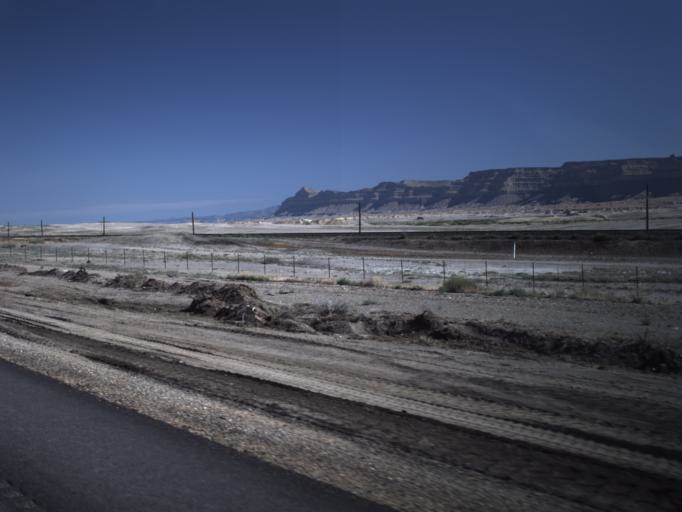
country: US
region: Utah
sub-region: Carbon County
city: East Carbon City
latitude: 39.0271
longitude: -110.3009
